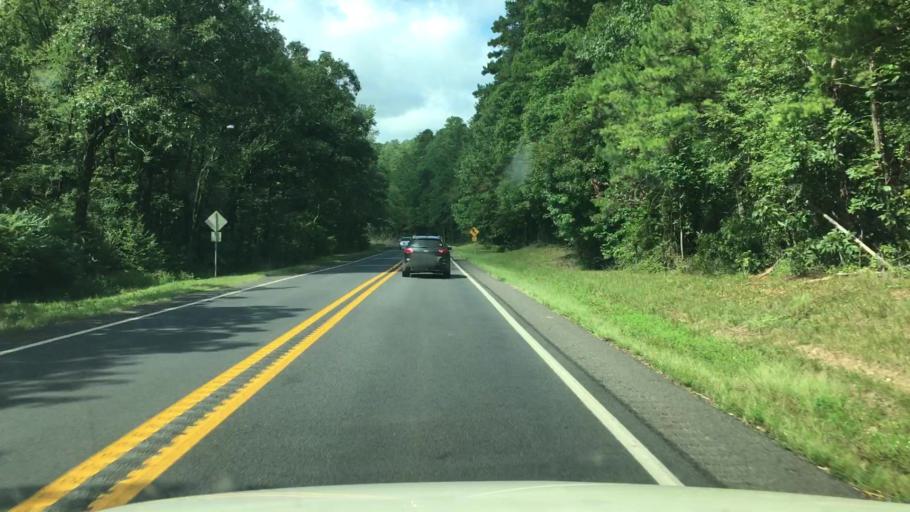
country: US
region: Arkansas
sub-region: Garland County
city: Lake Hamilton
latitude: 34.3556
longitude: -93.1808
